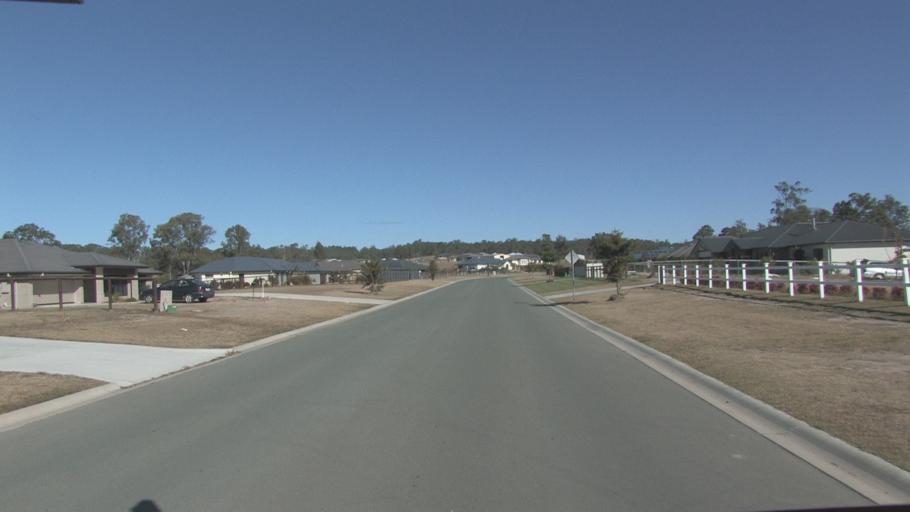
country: AU
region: Queensland
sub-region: Logan
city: Cedar Vale
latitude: -27.8700
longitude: 153.0481
